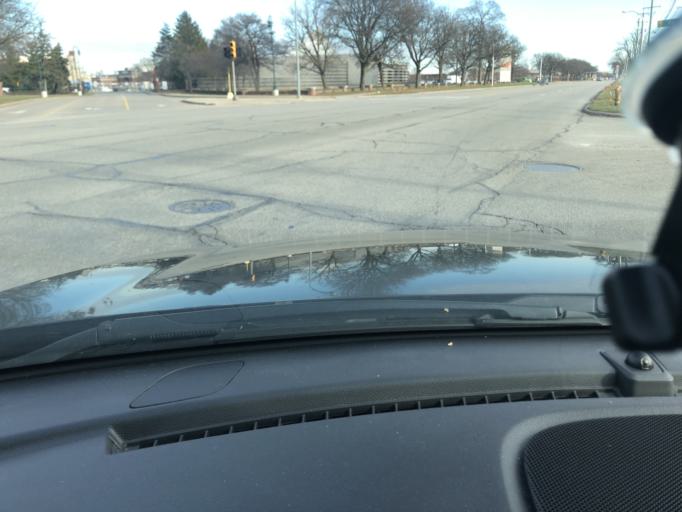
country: US
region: Michigan
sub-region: Wayne County
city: Dearborn Heights
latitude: 42.3025
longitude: -83.2396
